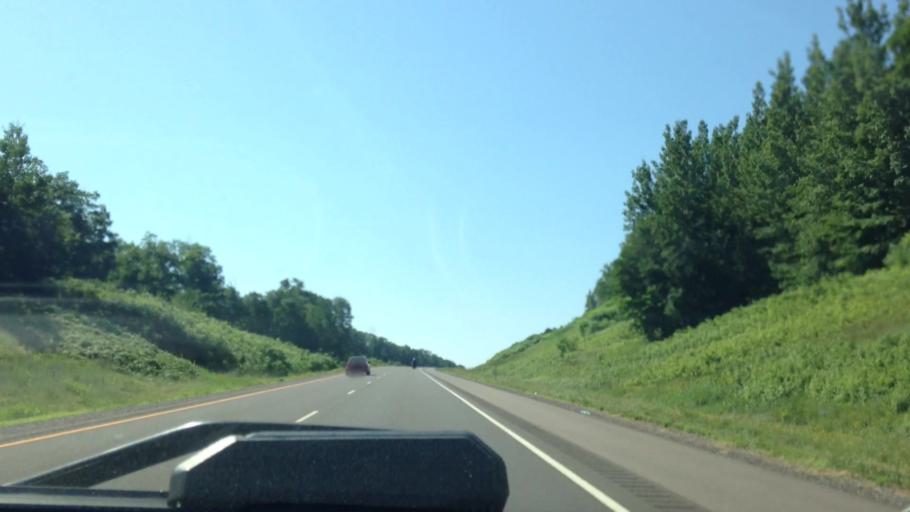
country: US
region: Wisconsin
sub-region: Washburn County
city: Spooner
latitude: 46.0079
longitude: -91.8354
